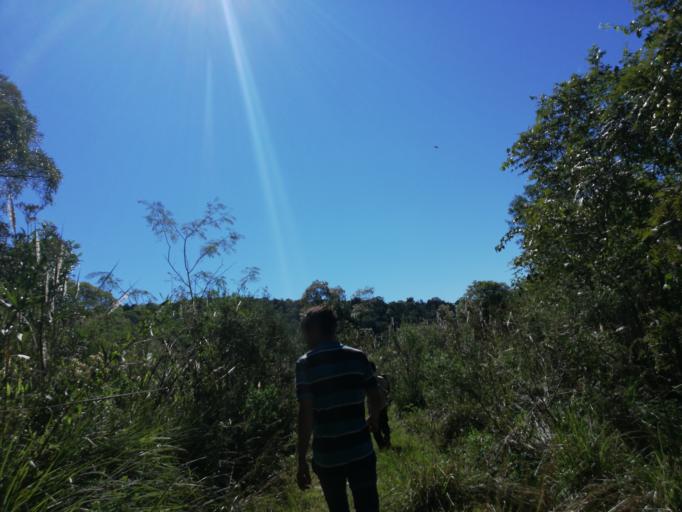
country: AR
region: Misiones
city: El Soberbio
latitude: -27.0608
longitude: -54.3755
